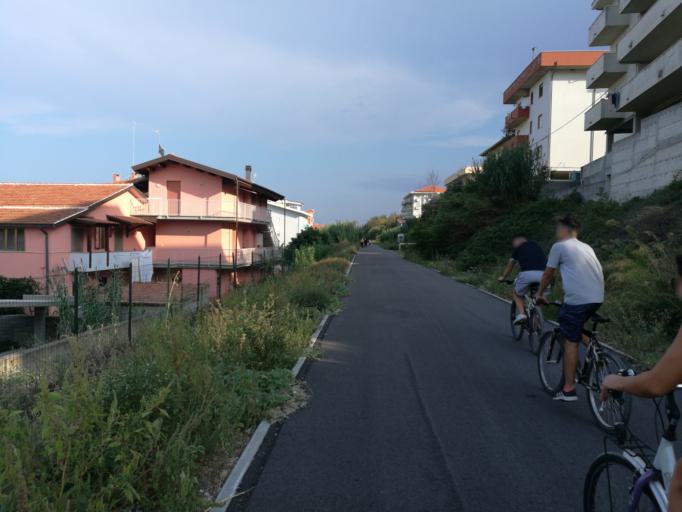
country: IT
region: Abruzzo
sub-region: Provincia di Chieti
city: Fossacesia
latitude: 42.2498
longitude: 14.5107
